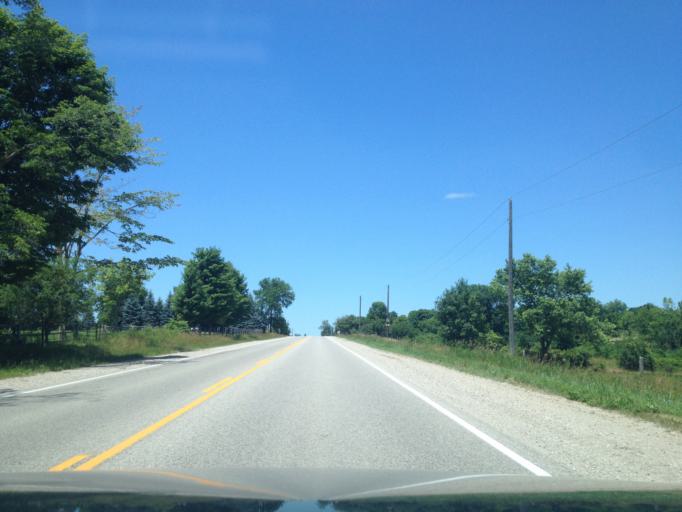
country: CA
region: Ontario
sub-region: Wellington County
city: Guelph
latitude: 43.6311
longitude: -80.2359
